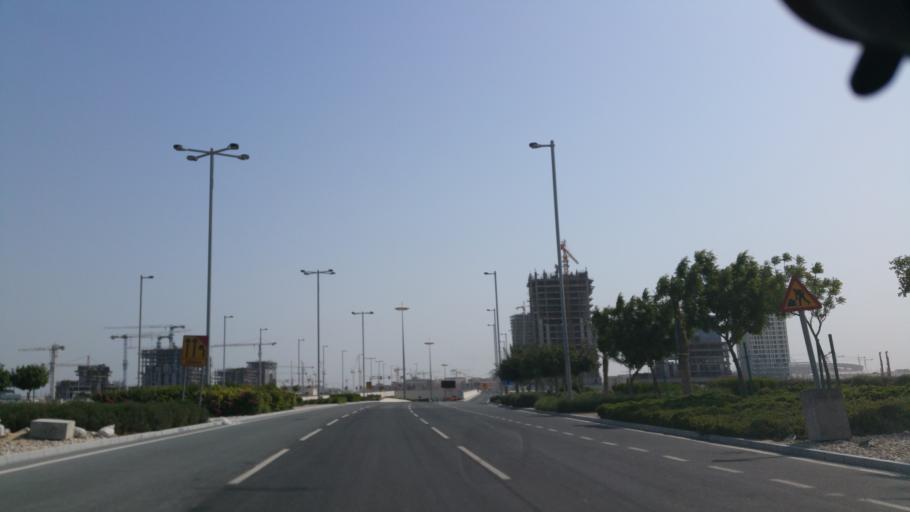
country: QA
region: Baladiyat Umm Salal
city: Umm Salal Muhammad
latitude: 25.4327
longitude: 51.5141
